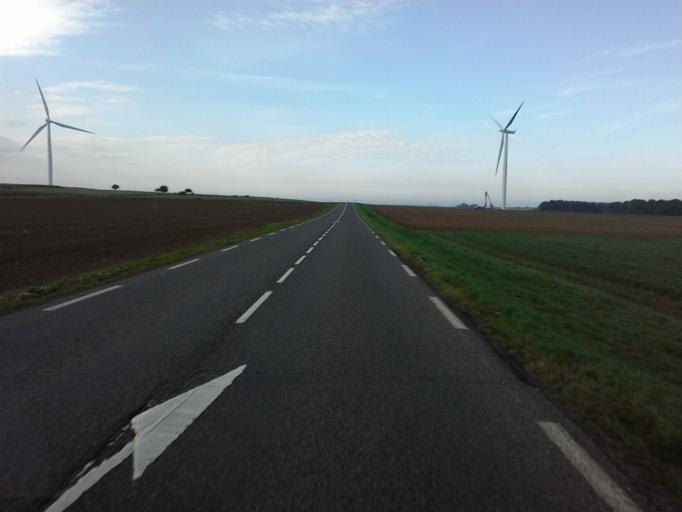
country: FR
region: Lorraine
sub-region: Departement de Meurthe-et-Moselle
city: Longuyon
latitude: 49.4962
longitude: 5.6203
